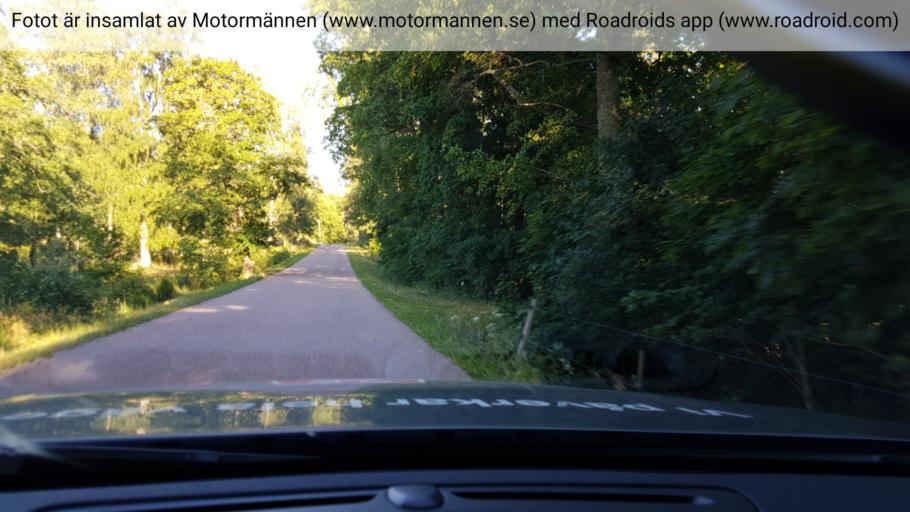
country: SE
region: Vaestmanland
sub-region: Surahammars Kommun
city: Ramnas
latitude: 59.6943
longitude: 16.0758
